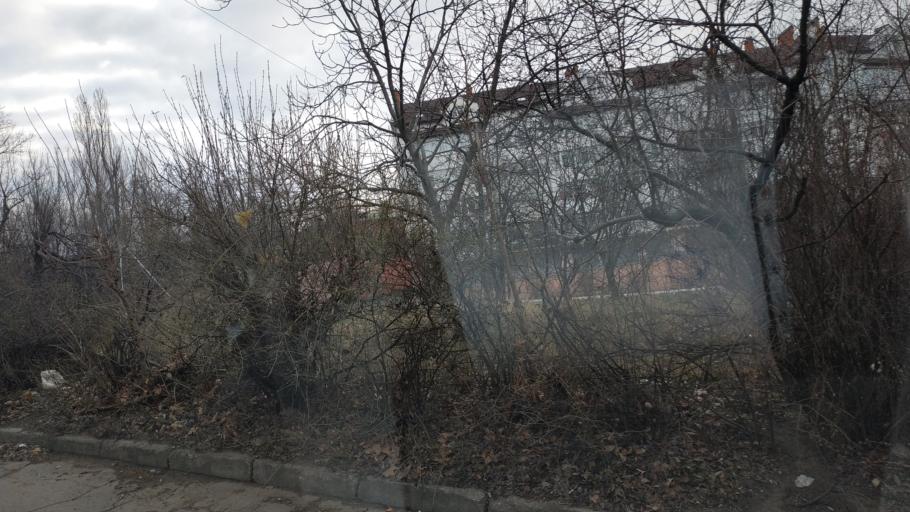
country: MD
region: Chisinau
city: Vatra
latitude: 47.0260
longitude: 28.7848
